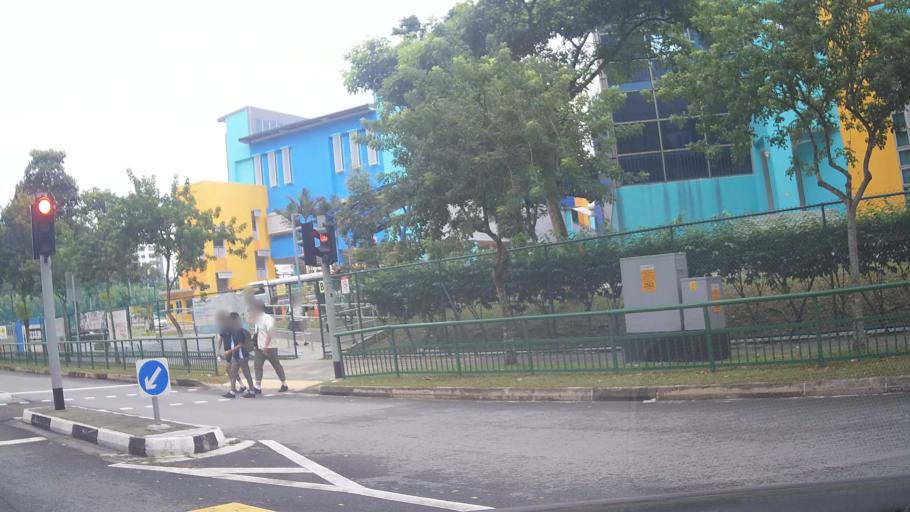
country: MY
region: Johor
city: Johor Bahru
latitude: 1.4469
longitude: 103.8031
